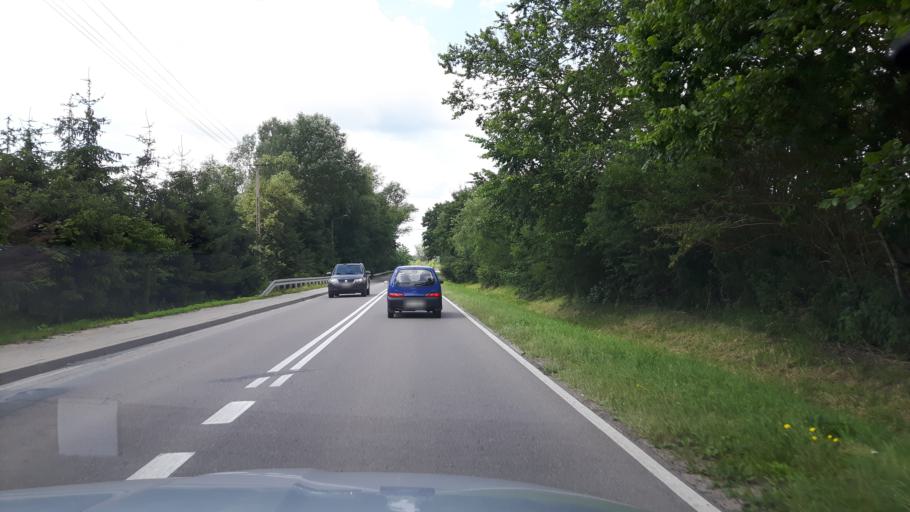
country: PL
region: Masovian Voivodeship
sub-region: Powiat ostrowski
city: Brok
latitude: 52.7013
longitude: 21.8765
